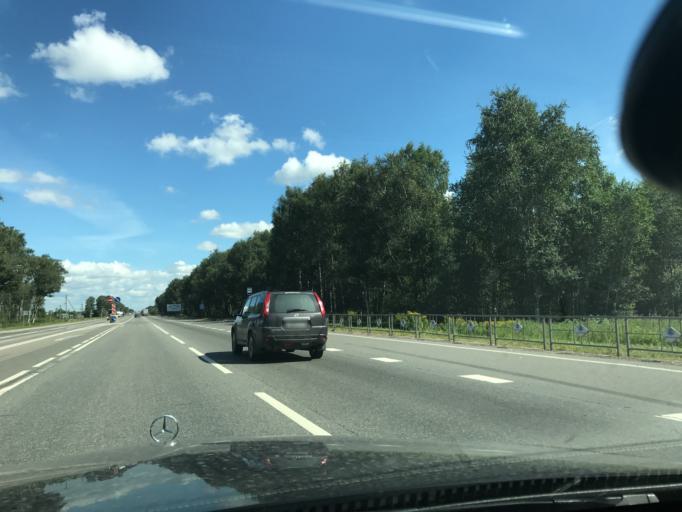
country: RU
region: Nizjnij Novgorod
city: Babino
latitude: 56.3048
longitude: 43.6335
